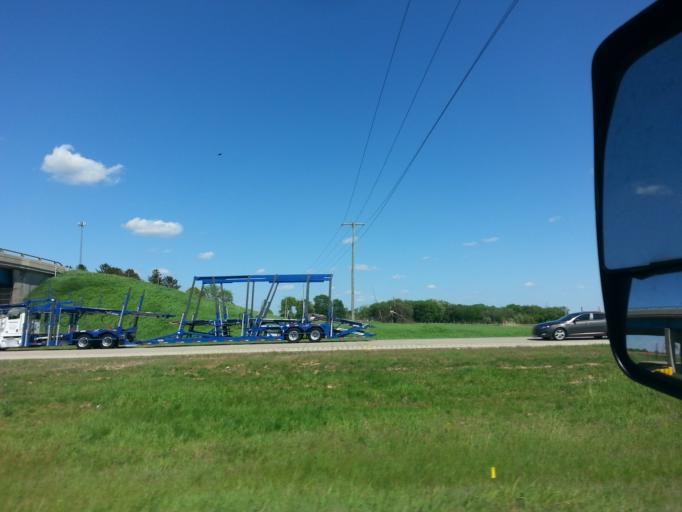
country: US
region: Illinois
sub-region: Winnebago County
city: Cherry Valley
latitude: 42.1730
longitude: -89.0239
